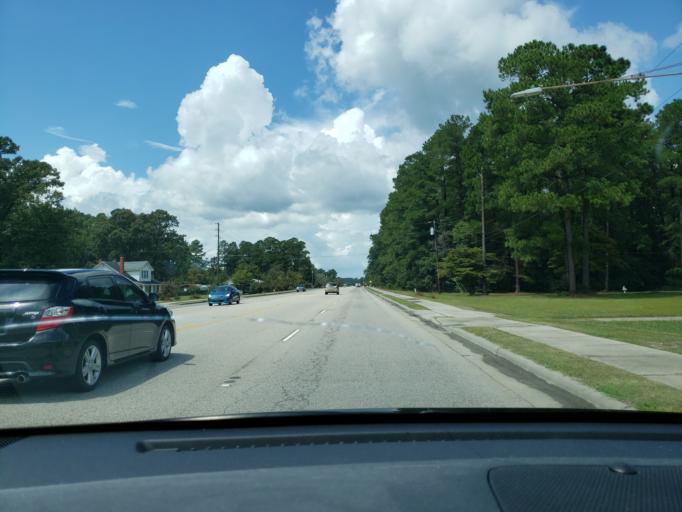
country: US
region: North Carolina
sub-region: Bladen County
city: Elizabethtown
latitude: 34.6510
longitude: -78.7139
